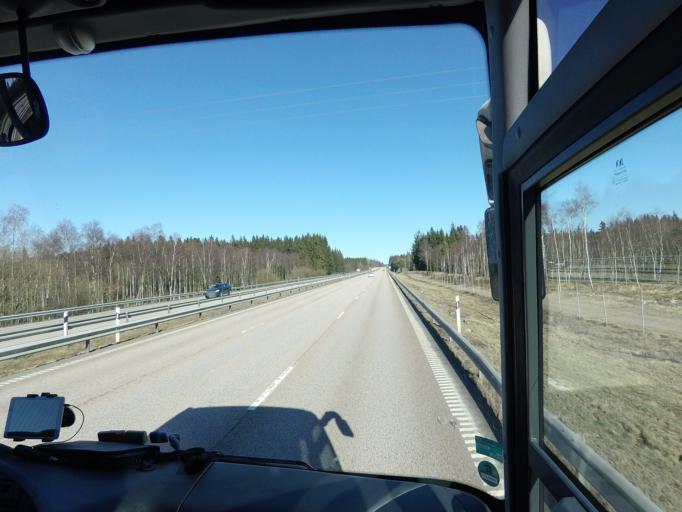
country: SE
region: Skane
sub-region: Bastads Kommun
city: Bastad
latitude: 56.3616
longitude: 12.9354
